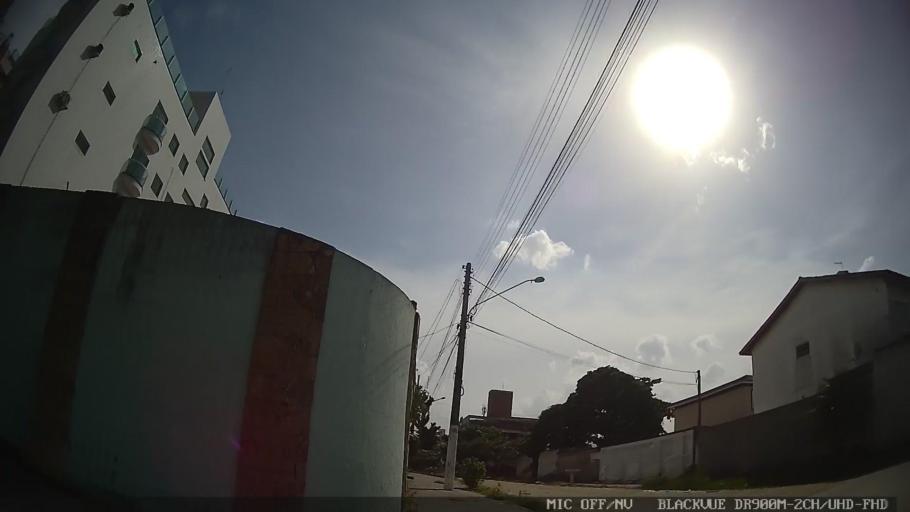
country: BR
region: Sao Paulo
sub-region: Guaruja
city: Guaruja
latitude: -23.9815
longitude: -46.2049
